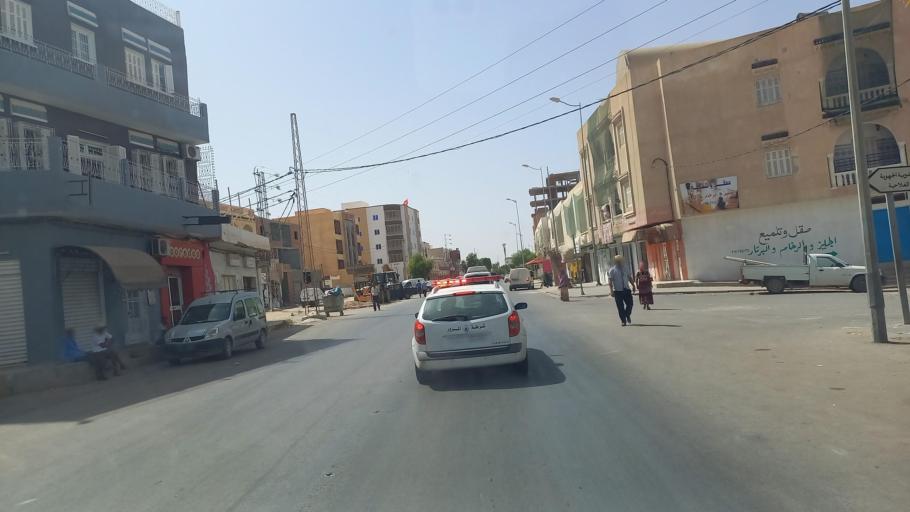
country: TN
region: Madanin
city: Medenine
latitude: 33.3331
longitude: 10.4855
